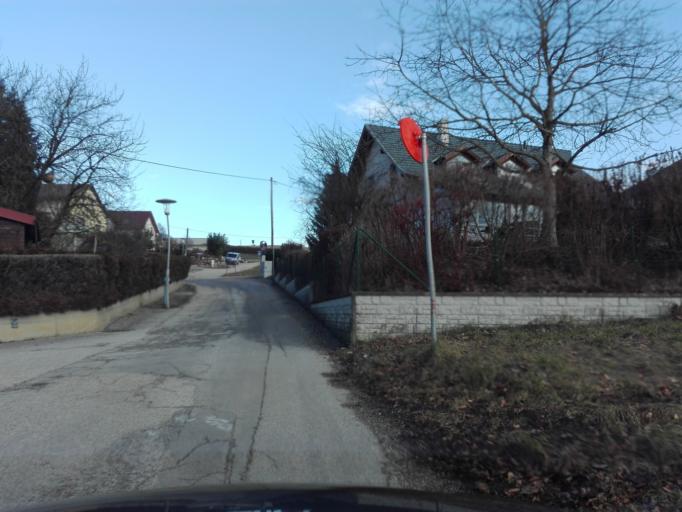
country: AT
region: Upper Austria
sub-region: Politischer Bezirk Perg
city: Perg
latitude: 48.2682
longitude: 14.5887
